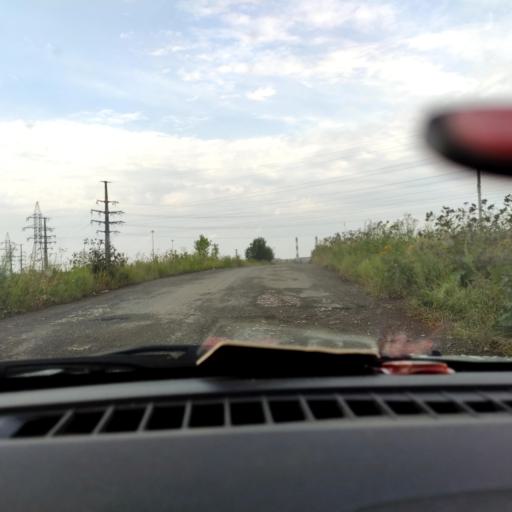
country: RU
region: Perm
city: Kondratovo
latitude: 57.9407
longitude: 56.1604
